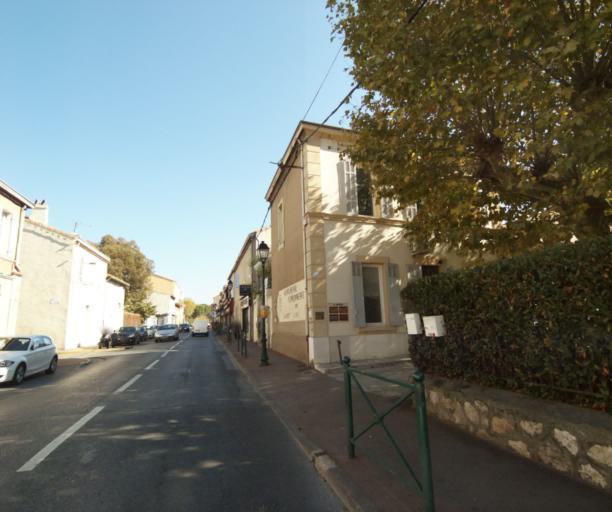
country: FR
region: Provence-Alpes-Cote d'Azur
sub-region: Departement des Bouches-du-Rhone
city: Plan-de-Cuques
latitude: 43.3466
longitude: 5.4627
